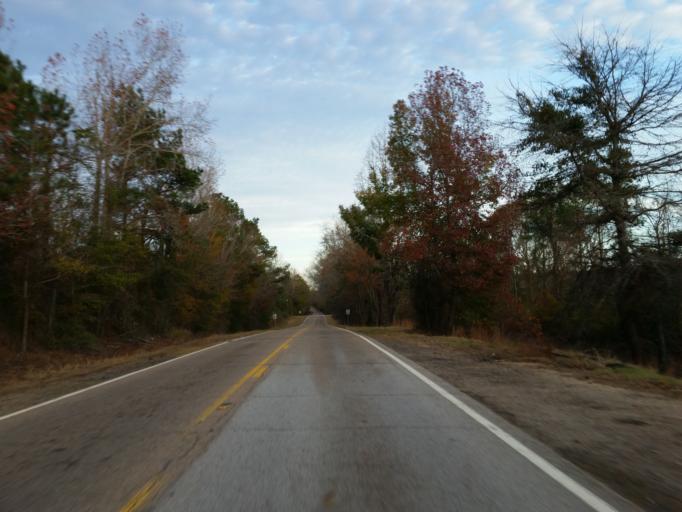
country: US
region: Alabama
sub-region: Sumter County
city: York
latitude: 32.4239
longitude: -88.4337
